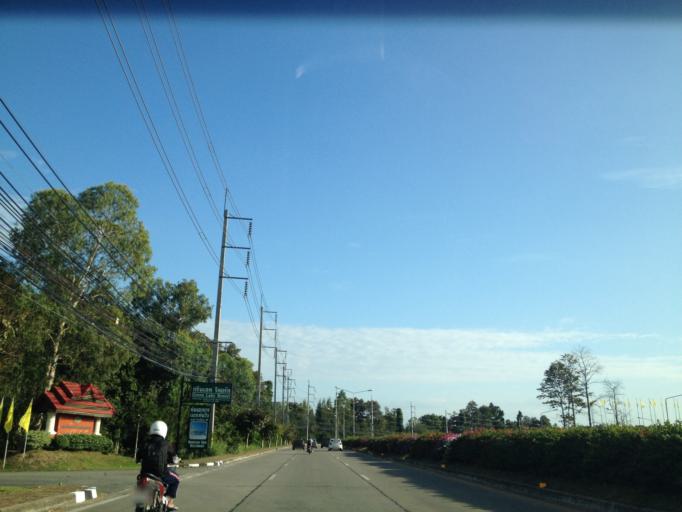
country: TH
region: Chiang Mai
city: Chiang Mai
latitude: 18.8280
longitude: 98.9645
